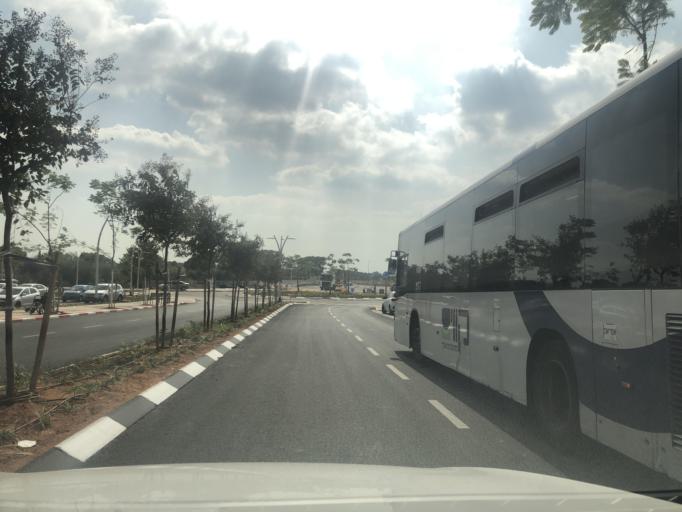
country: IL
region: Tel Aviv
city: Or Yehuda
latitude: 32.0436
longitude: 34.8430
